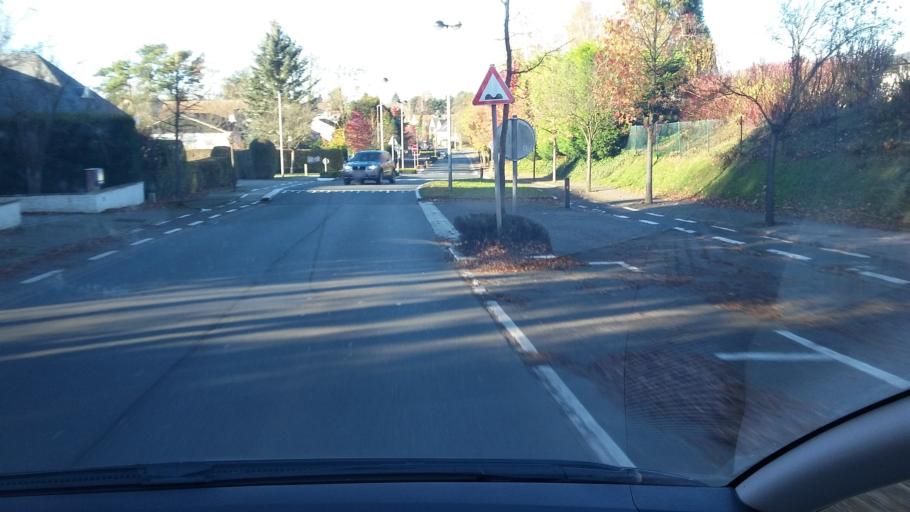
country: BE
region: Wallonia
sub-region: Province du Brabant Wallon
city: Waterloo
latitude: 50.7019
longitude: 4.4218
